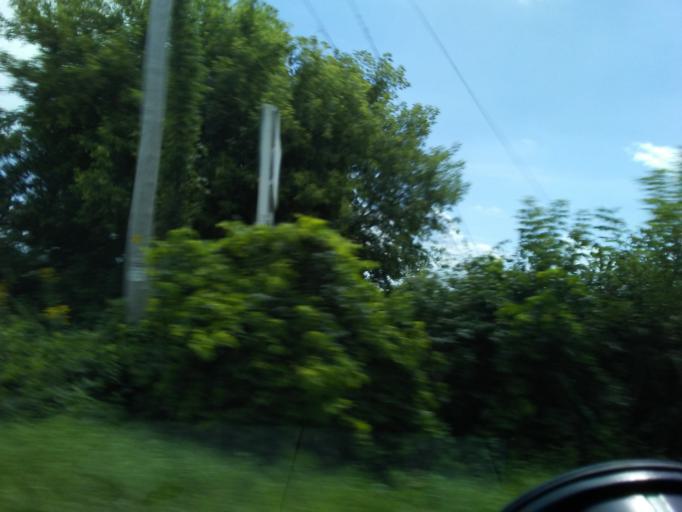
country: US
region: Wisconsin
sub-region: Dane County
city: Verona
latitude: 43.0162
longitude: -89.5436
